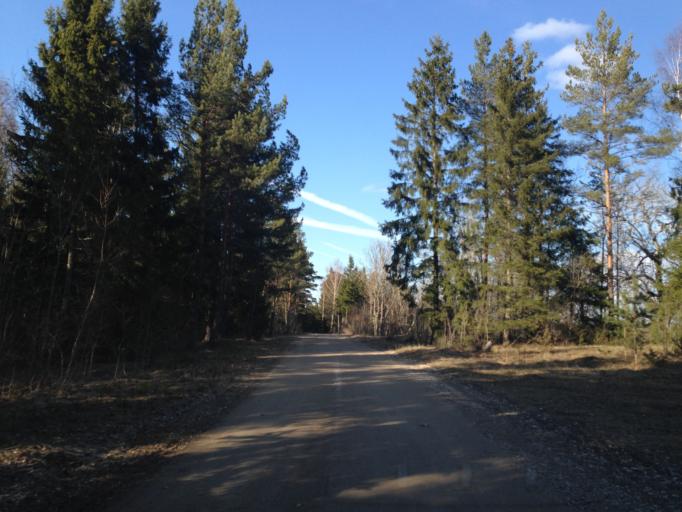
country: EE
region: Harju
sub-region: Nissi vald
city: Turba
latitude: 59.1001
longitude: 24.1530
